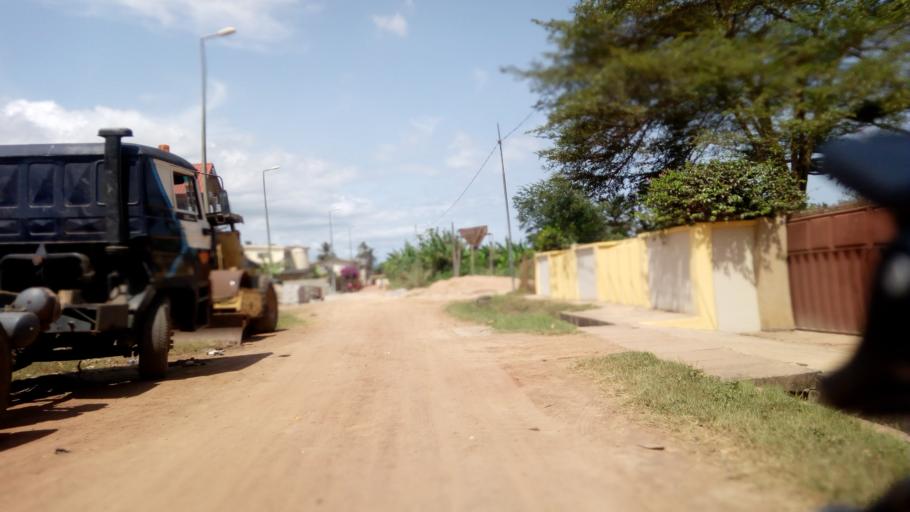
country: GH
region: Central
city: Cape Coast
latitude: 5.1321
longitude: -1.2809
